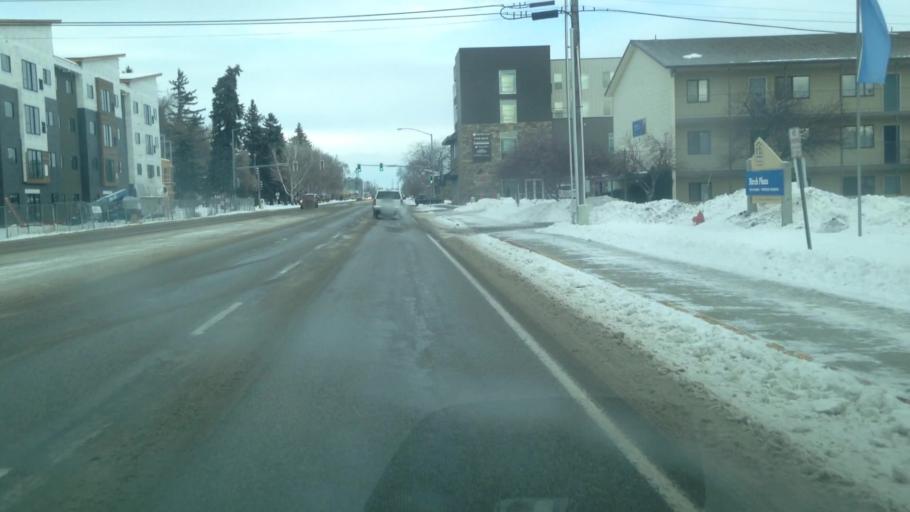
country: US
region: Idaho
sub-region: Madison County
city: Rexburg
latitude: 43.8205
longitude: -111.7895
